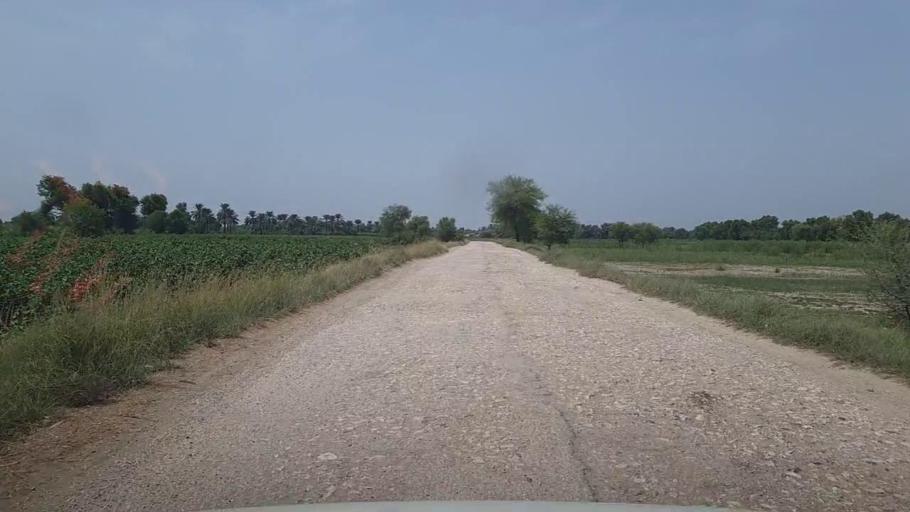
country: PK
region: Sindh
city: Pano Aqil
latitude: 27.8498
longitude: 69.1426
